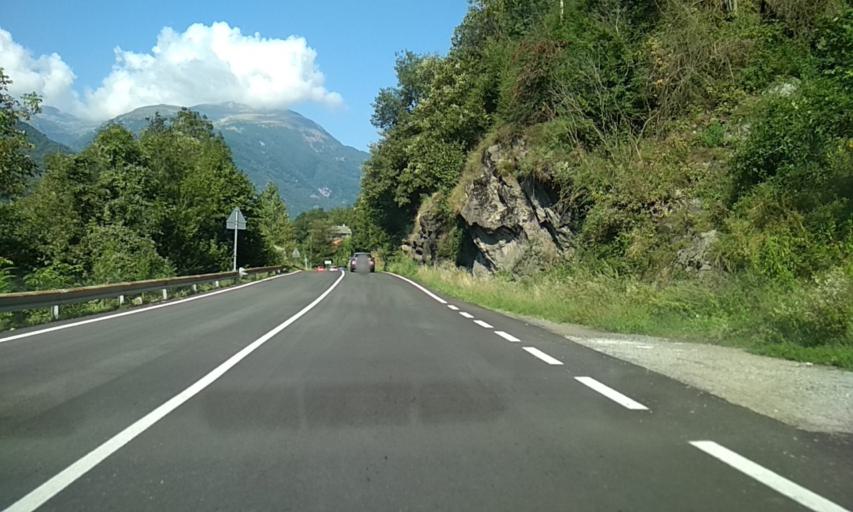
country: IT
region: Piedmont
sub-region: Provincia di Torino
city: Ribordone
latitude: 45.4078
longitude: 7.4939
